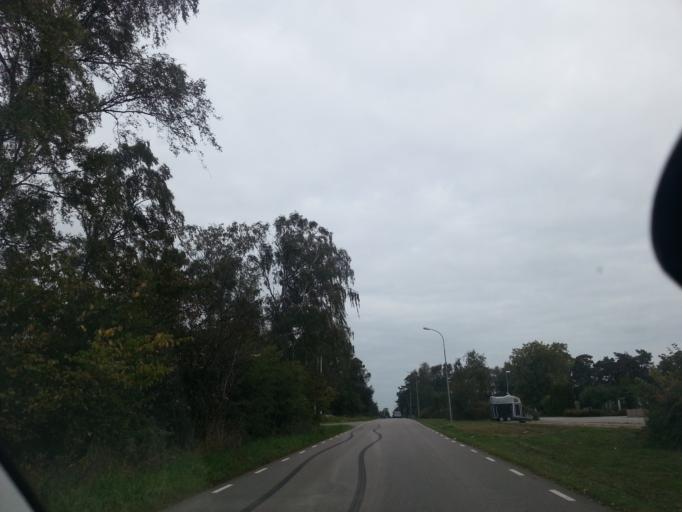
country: SE
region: Skane
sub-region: Landskrona
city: Asmundtorp
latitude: 55.8502
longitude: 12.9109
